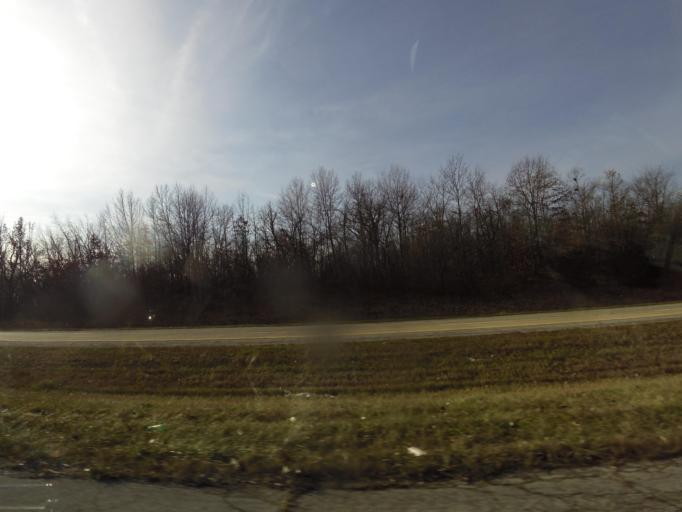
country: US
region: Illinois
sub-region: De Witt County
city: Clinton
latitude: 40.1306
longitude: -88.9683
